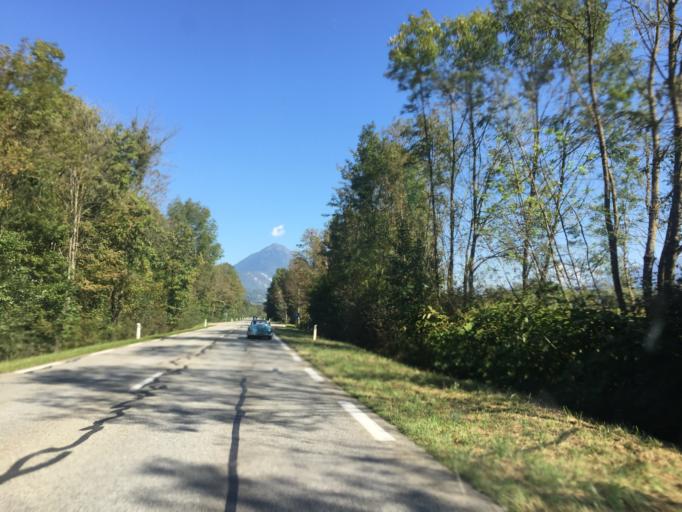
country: FR
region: Rhone-Alpes
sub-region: Departement de la Savoie
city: Gresy-sur-Isere
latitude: 45.5957
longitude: 6.2756
